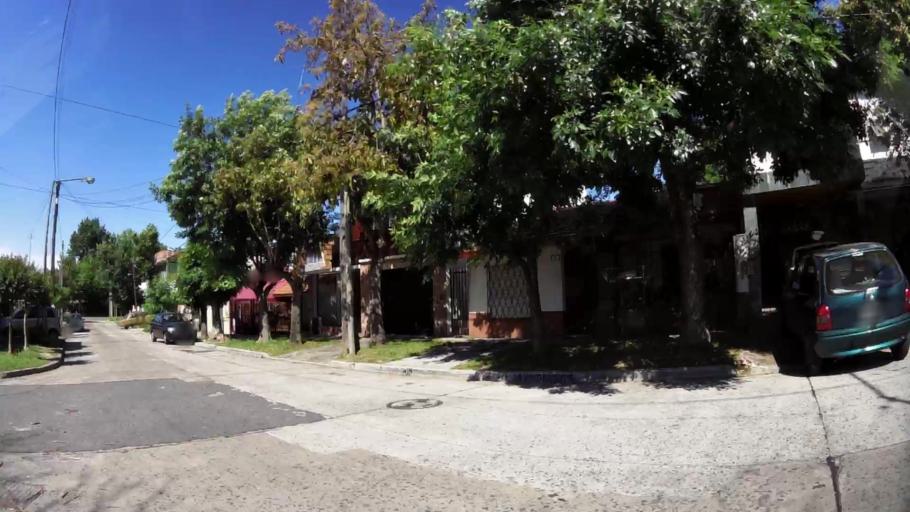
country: AR
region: Buenos Aires
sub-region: Partido de General San Martin
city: General San Martin
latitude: -34.5396
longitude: -58.5718
